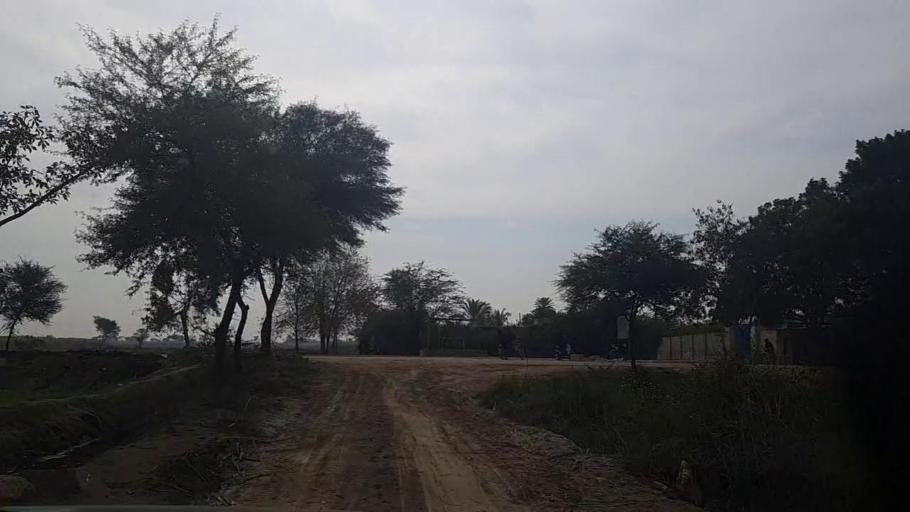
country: PK
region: Sindh
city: Sakrand
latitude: 26.2262
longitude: 68.2970
